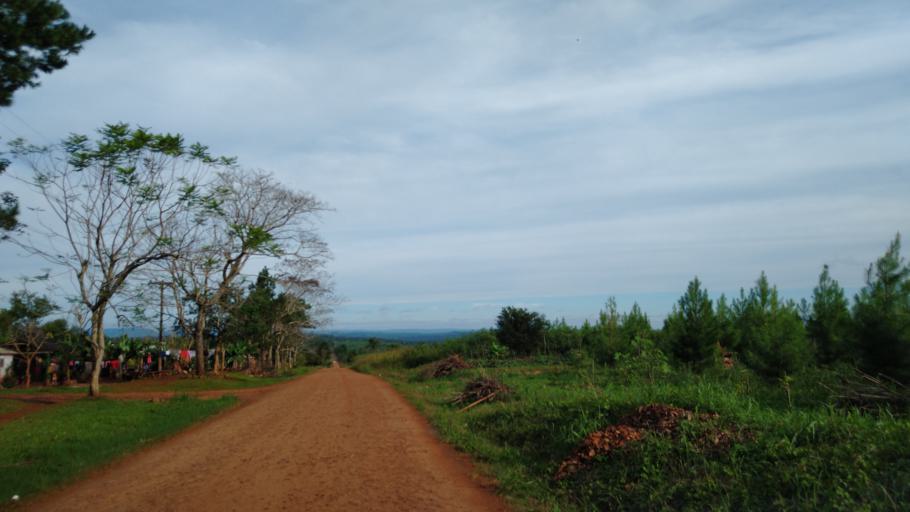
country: AR
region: Misiones
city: Capiovi
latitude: -26.9451
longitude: -55.0965
